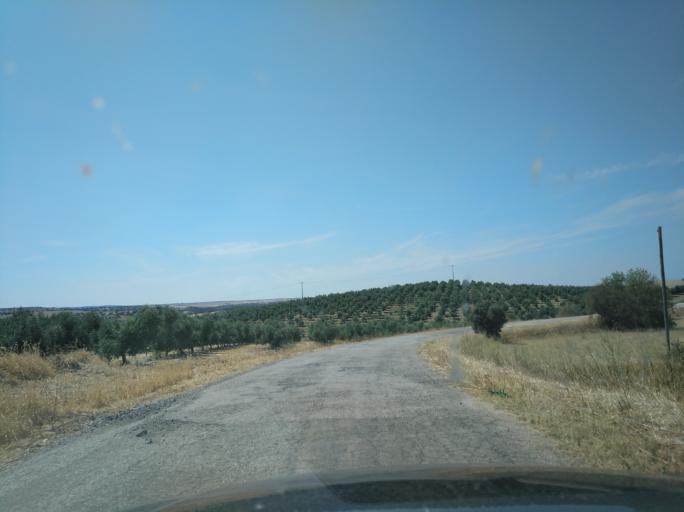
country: PT
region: Portalegre
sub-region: Campo Maior
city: Campo Maior
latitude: 38.9830
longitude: -7.0969
